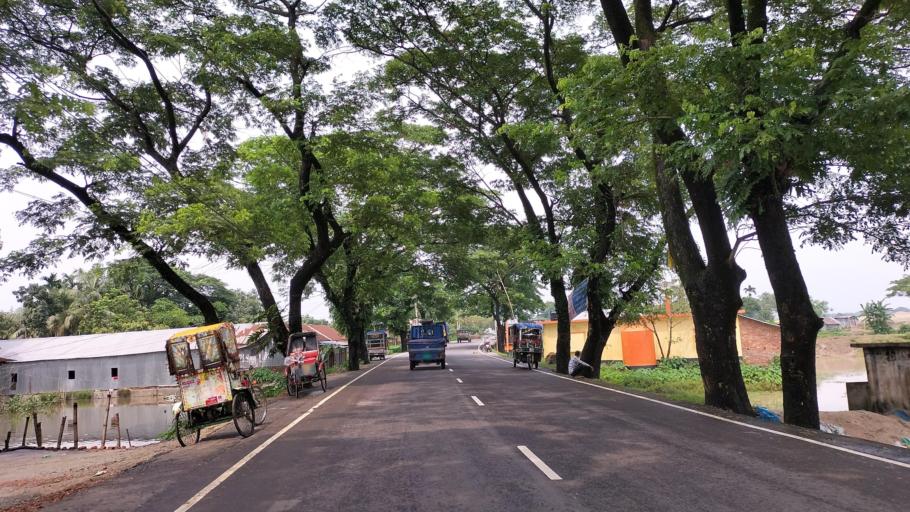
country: BD
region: Dhaka
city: Netrakona
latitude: 24.9008
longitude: 90.7541
